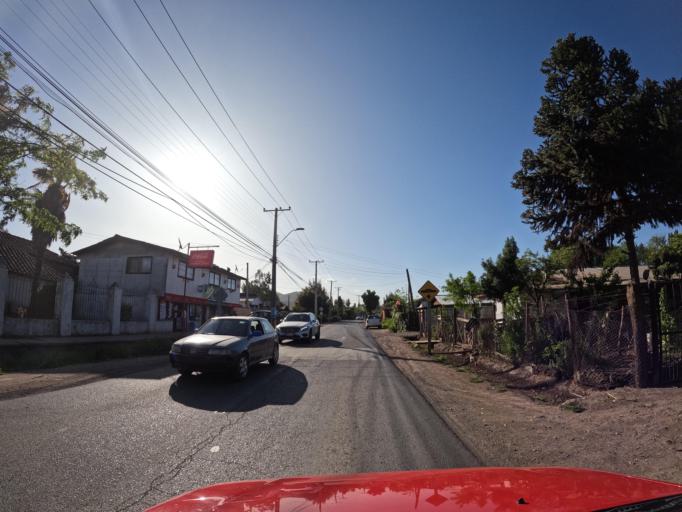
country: CL
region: O'Higgins
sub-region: Provincia de Colchagua
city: Santa Cruz
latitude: -34.7215
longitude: -71.2848
